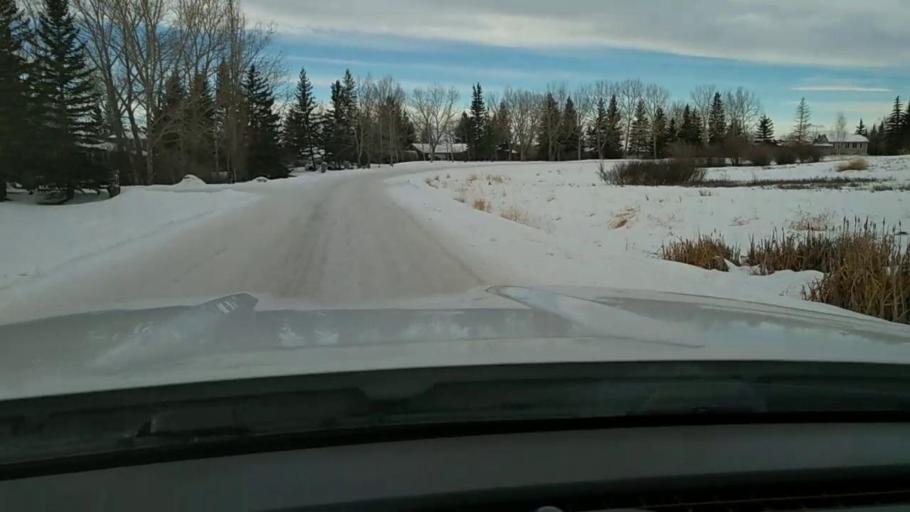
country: CA
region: Alberta
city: Calgary
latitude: 51.1165
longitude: -114.2644
